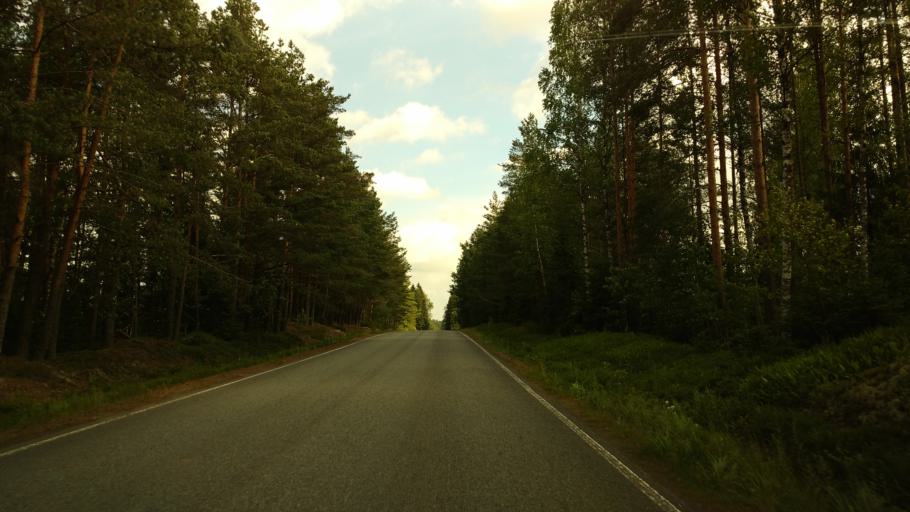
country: FI
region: Haeme
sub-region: Forssa
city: Ypaejae
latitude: 60.7498
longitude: 23.2048
